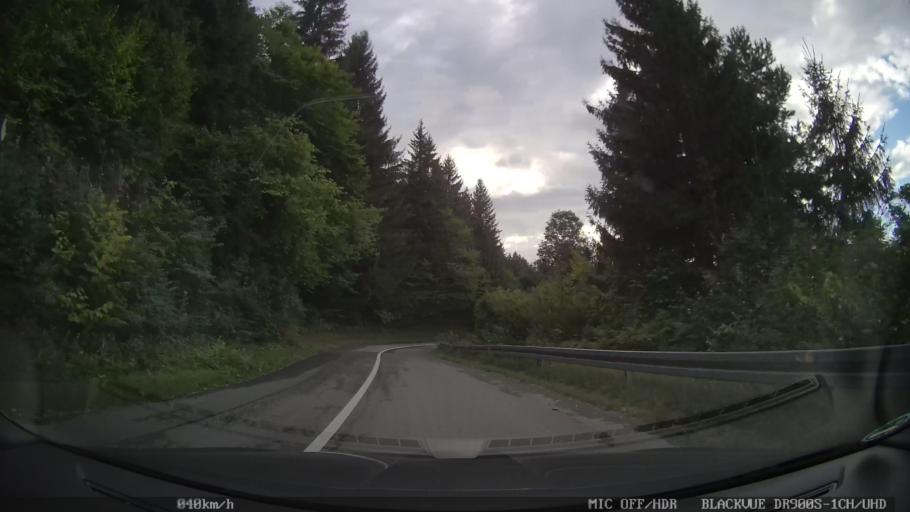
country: HR
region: Karlovacka
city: Plaski
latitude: 44.9931
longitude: 15.4581
